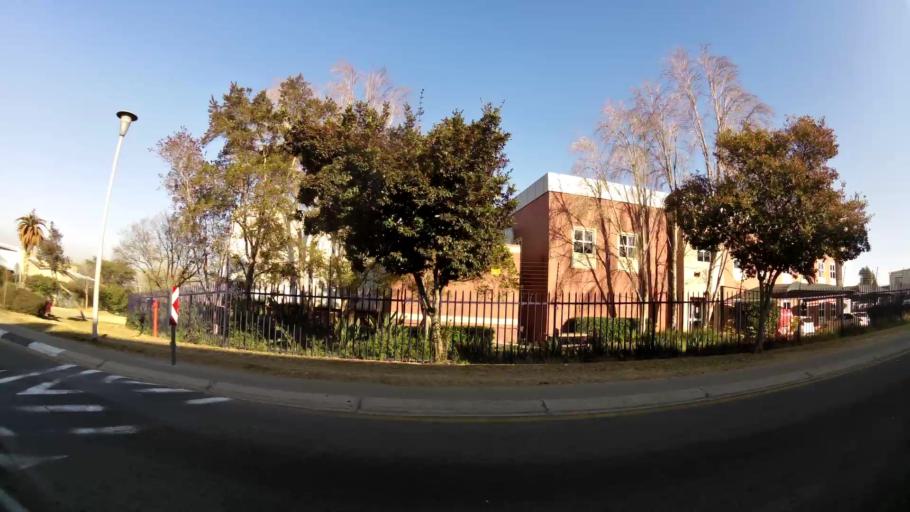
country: ZA
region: Gauteng
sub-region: City of Johannesburg Metropolitan Municipality
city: Modderfontein
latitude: -26.0721
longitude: 28.1162
